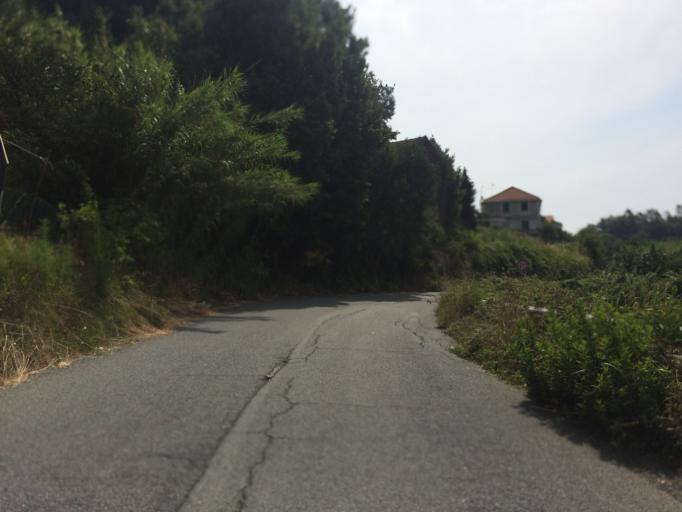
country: IT
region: Liguria
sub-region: Provincia di Savona
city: San Giovanni
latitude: 44.3917
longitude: 8.5111
